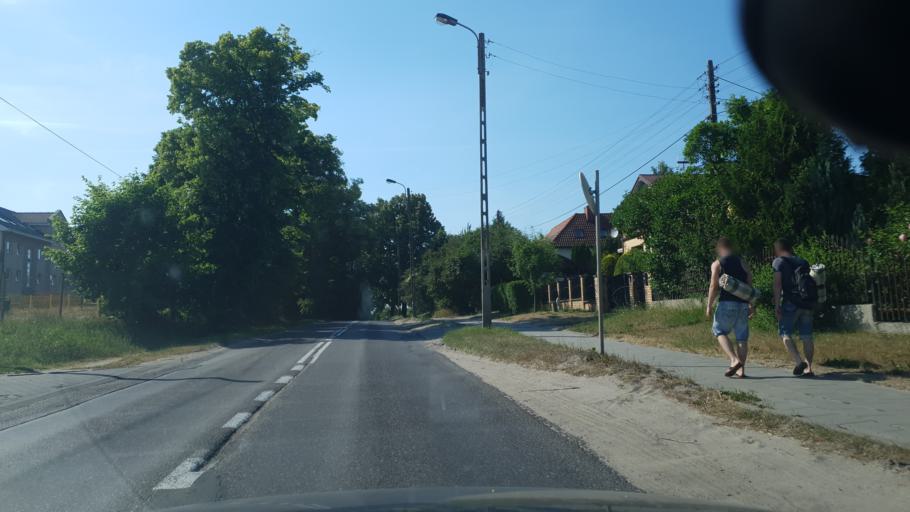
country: PL
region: Pomeranian Voivodeship
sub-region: Gdynia
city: Wielki Kack
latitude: 54.4354
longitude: 18.4652
